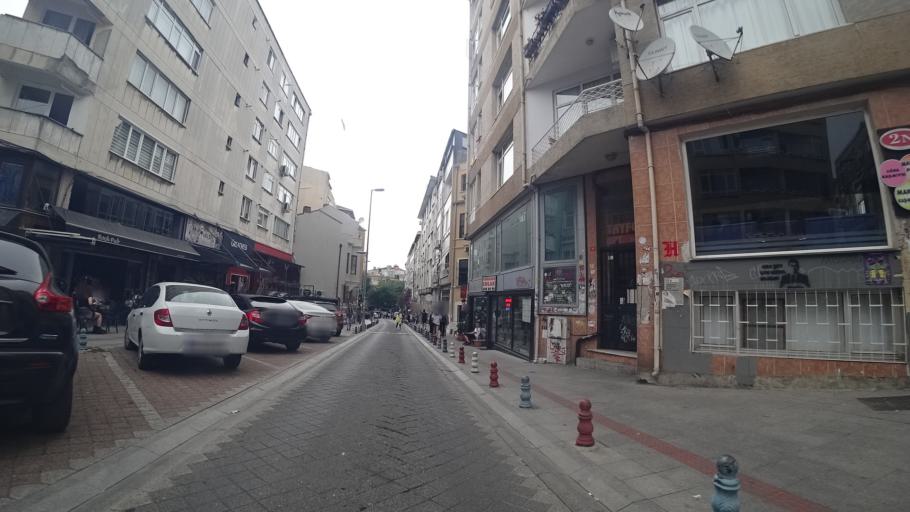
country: TR
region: Istanbul
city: UEskuedar
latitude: 40.9851
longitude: 29.0267
